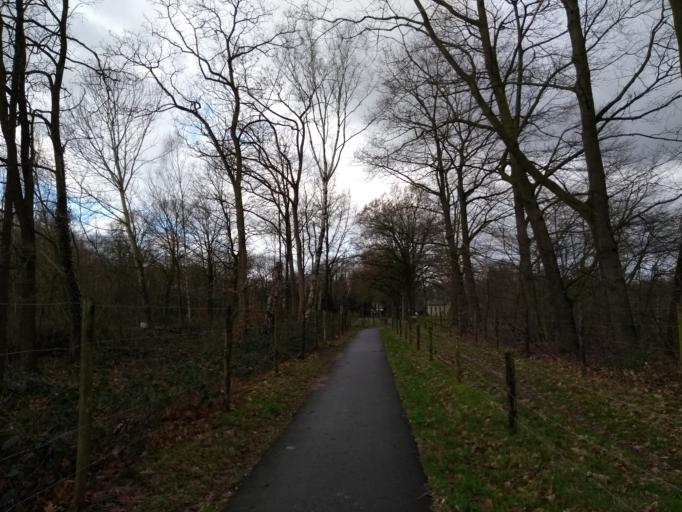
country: NL
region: Overijssel
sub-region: Gemeente Enschede
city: Enschede
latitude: 52.2467
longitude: 6.8824
